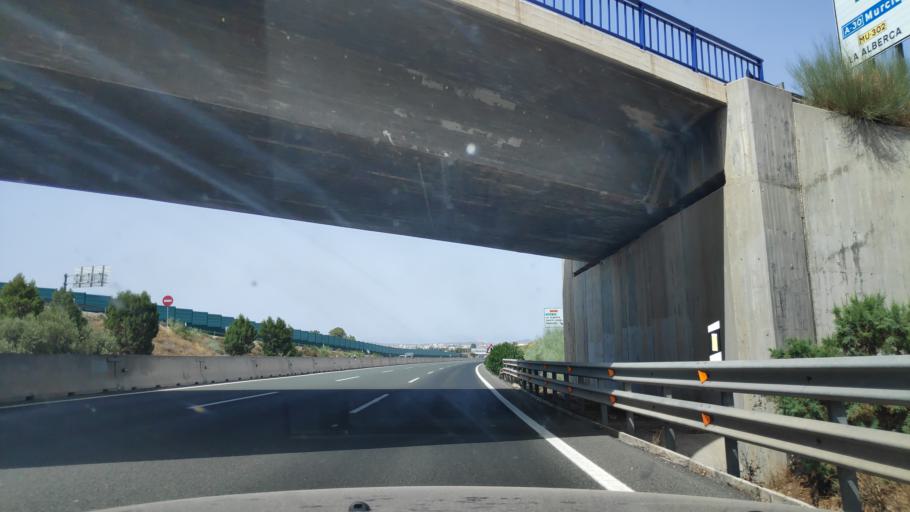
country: ES
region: Murcia
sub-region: Murcia
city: Murcia
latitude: 37.9356
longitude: -1.1532
